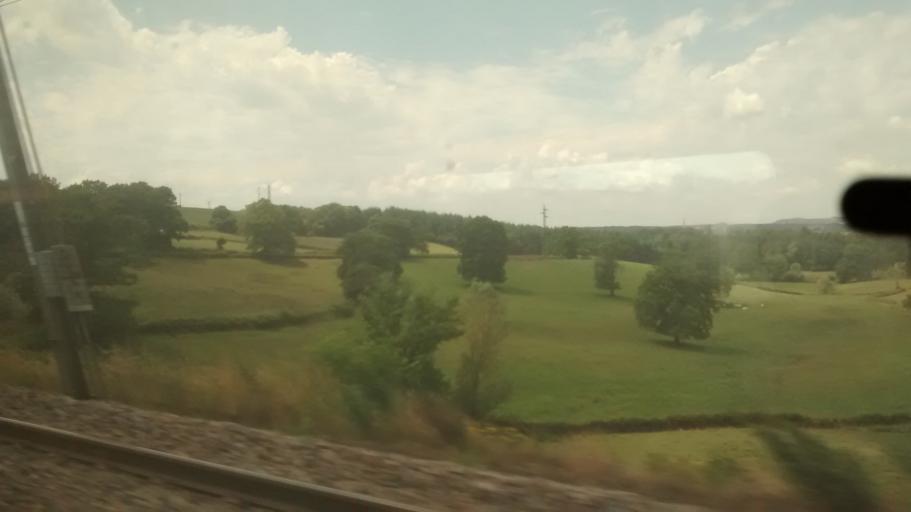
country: FR
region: Bourgogne
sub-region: Departement de Saone-et-Loire
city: Le Breuil
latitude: 46.7994
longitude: 4.4959
